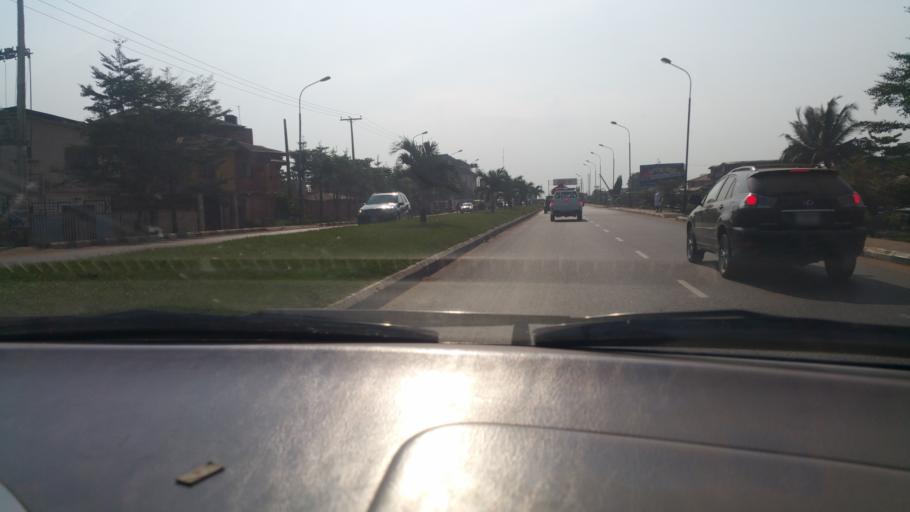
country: NG
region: Lagos
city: Ikotun
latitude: 6.5536
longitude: 3.2462
